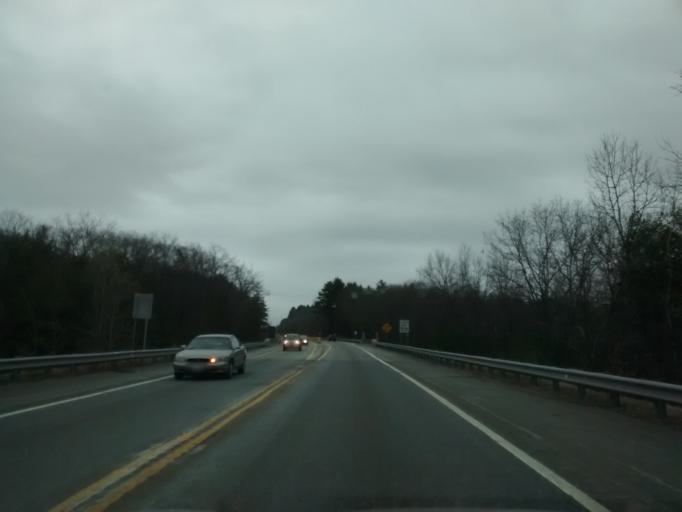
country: US
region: Massachusetts
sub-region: Worcester County
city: Athol
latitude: 42.5637
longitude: -72.2485
